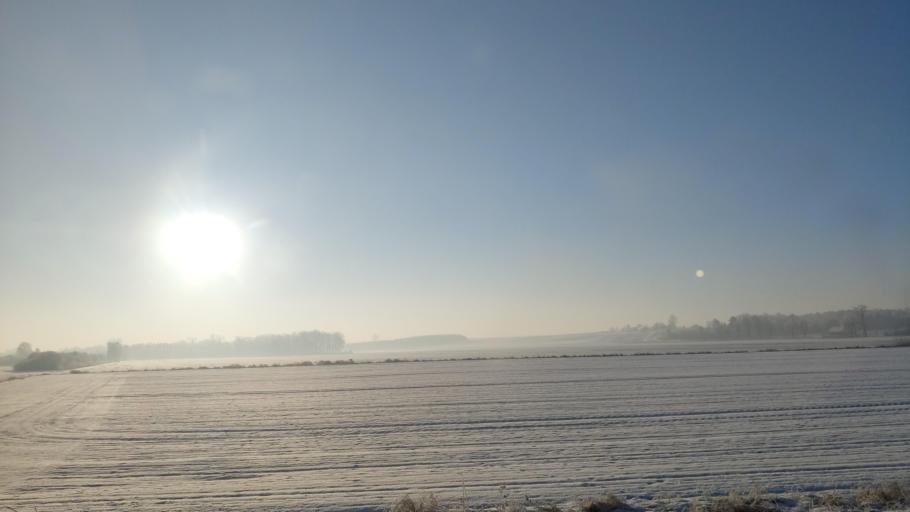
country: PL
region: Kujawsko-Pomorskie
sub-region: Powiat zninski
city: Barcin
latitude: 52.8749
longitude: 17.8618
